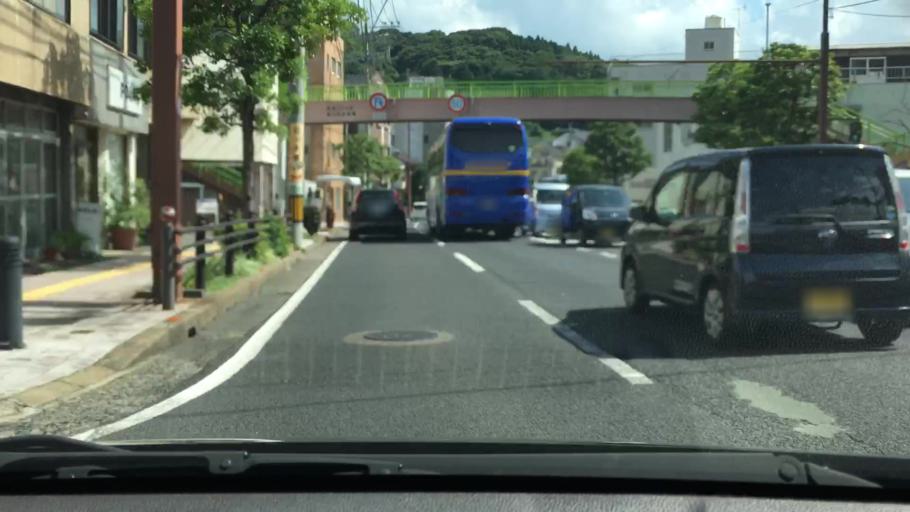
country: JP
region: Nagasaki
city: Sasebo
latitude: 33.1983
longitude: 129.7224
